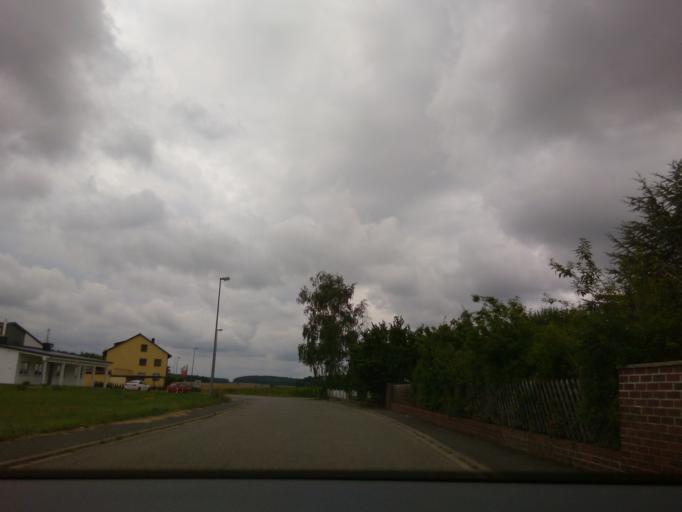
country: DE
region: Bavaria
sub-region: Regierungsbezirk Mittelfranken
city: Hochstadt an der Aisch
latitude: 49.6936
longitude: 10.7994
